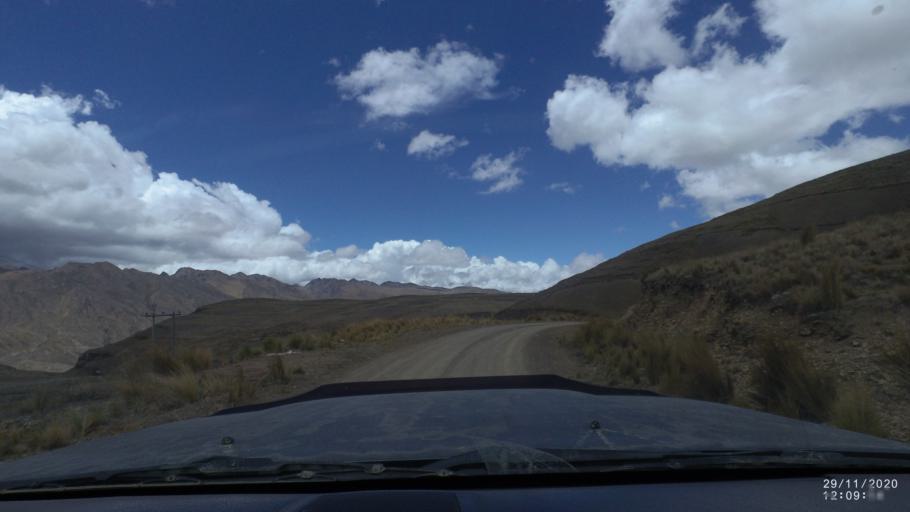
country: BO
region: Cochabamba
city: Cochabamba
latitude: -17.1316
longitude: -66.3030
